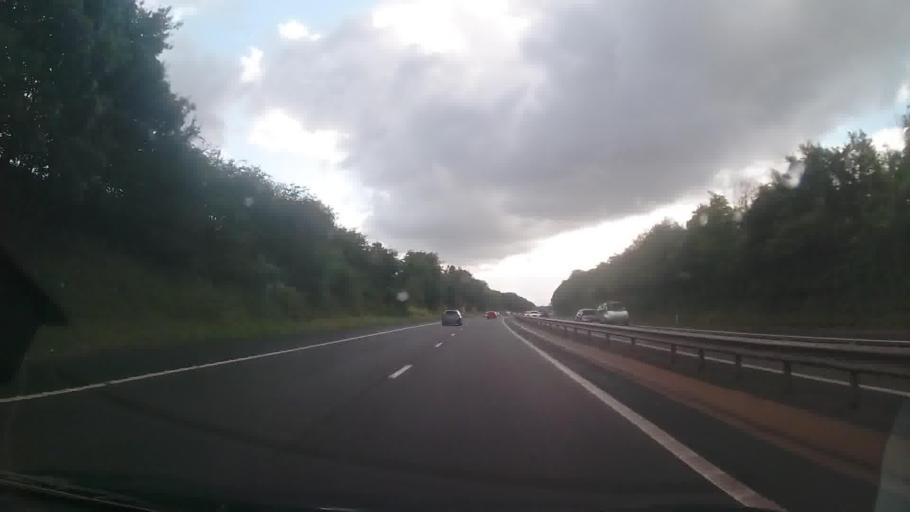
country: GB
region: England
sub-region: Telford and Wrekin
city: Wellington
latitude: 52.6899
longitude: -2.5262
